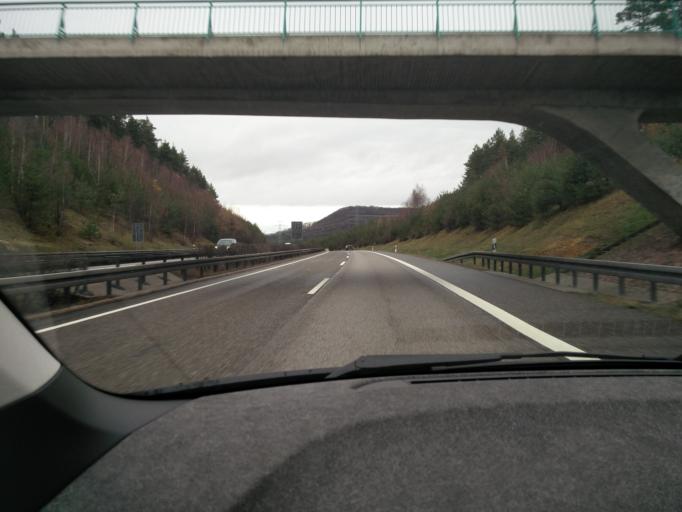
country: DE
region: Thuringia
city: Behringen
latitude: 50.7526
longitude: 11.0034
